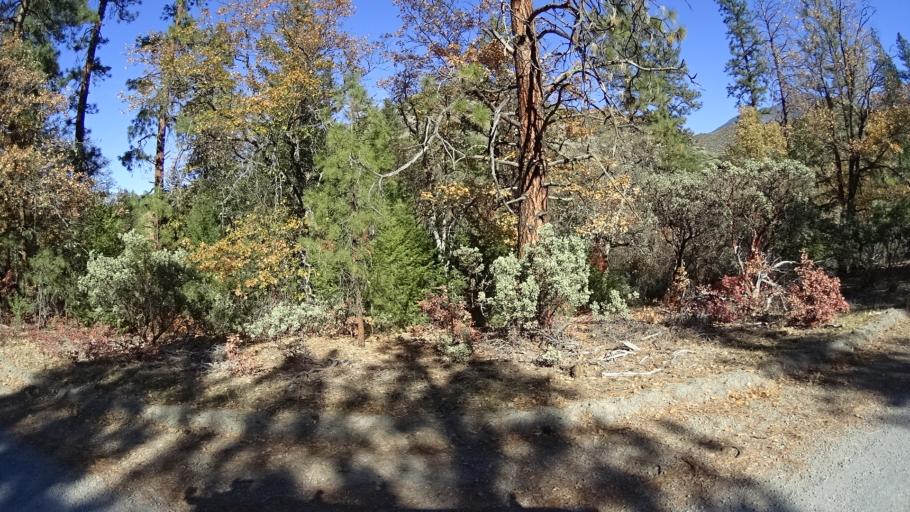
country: US
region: California
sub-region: Siskiyou County
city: Yreka
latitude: 41.8542
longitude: -122.7000
